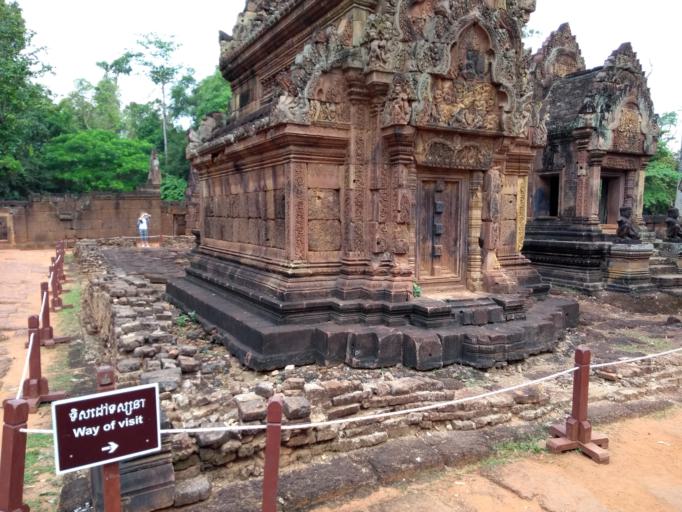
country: KH
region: Siem Reap
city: Siem Reap
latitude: 13.5988
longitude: 103.9631
